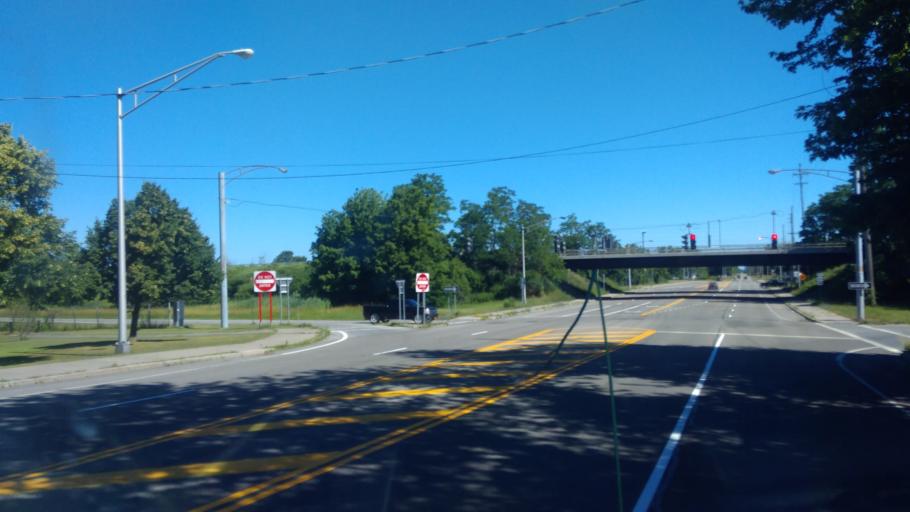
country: US
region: New York
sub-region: Monroe County
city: Webster
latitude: 43.2189
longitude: -77.4000
